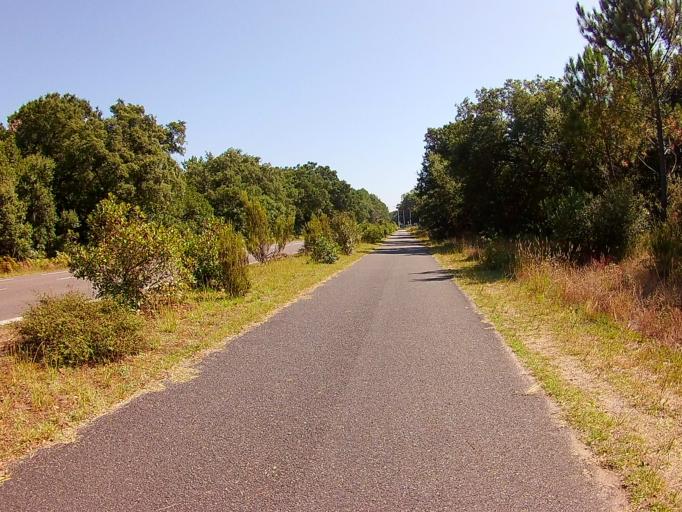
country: FR
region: Aquitaine
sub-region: Departement des Landes
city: Labenne
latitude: 43.5925
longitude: -1.4497
